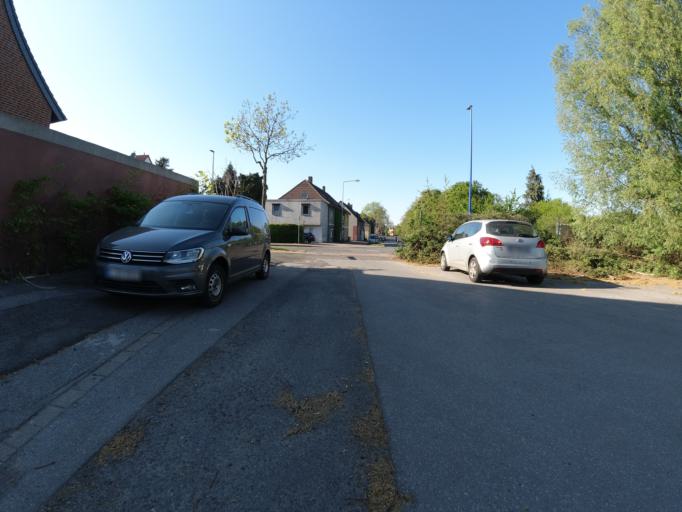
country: DE
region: North Rhine-Westphalia
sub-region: Regierungsbezirk Dusseldorf
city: Hochfeld
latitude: 51.3840
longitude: 6.7116
